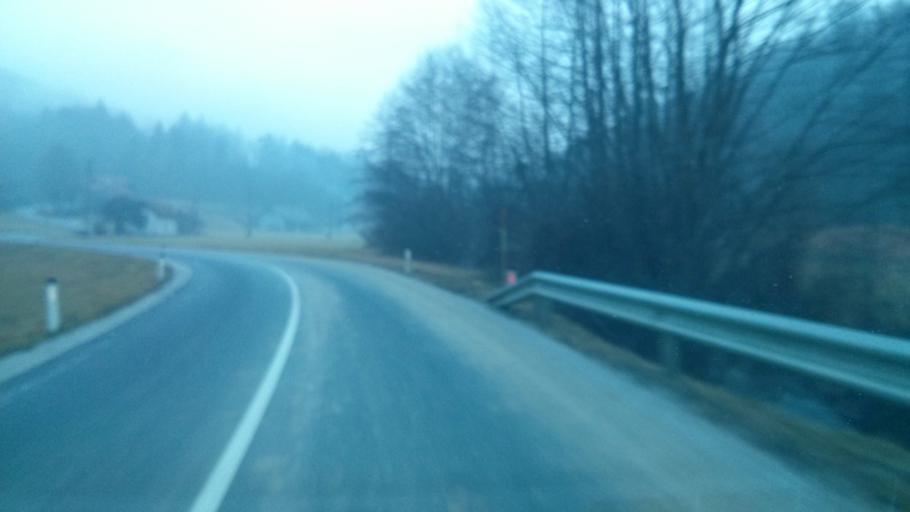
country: SI
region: Smartno pri Litiji
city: Smartno pri Litiji
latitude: 46.0407
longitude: 14.8558
